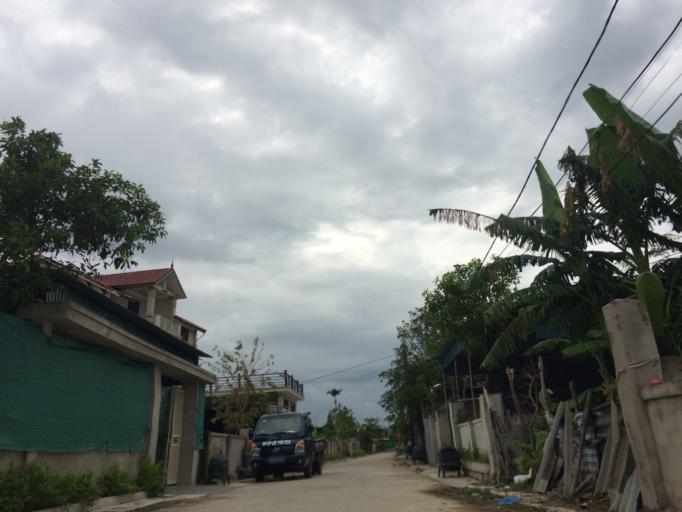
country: VN
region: Ha Tinh
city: Thach Ha
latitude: 18.3665
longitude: 105.8888
